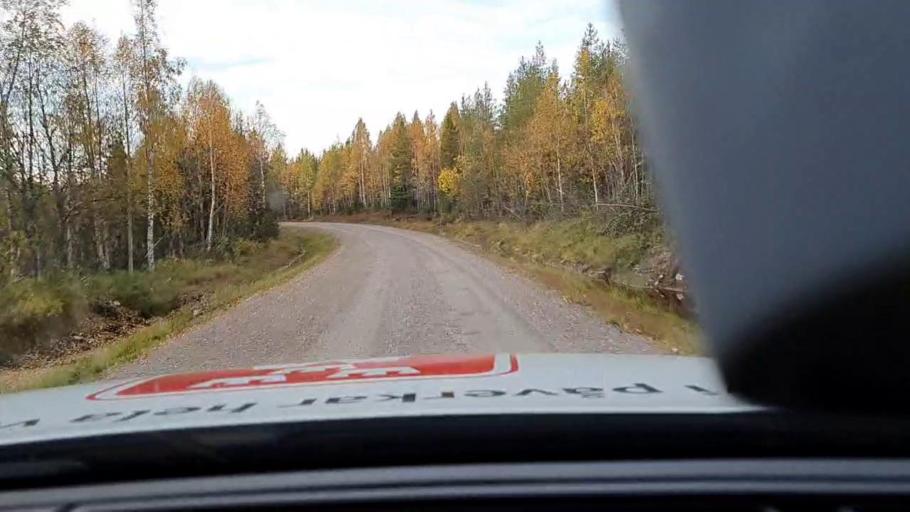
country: SE
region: Norrbotten
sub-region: Lulea Kommun
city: Ranea
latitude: 66.2678
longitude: 22.2598
